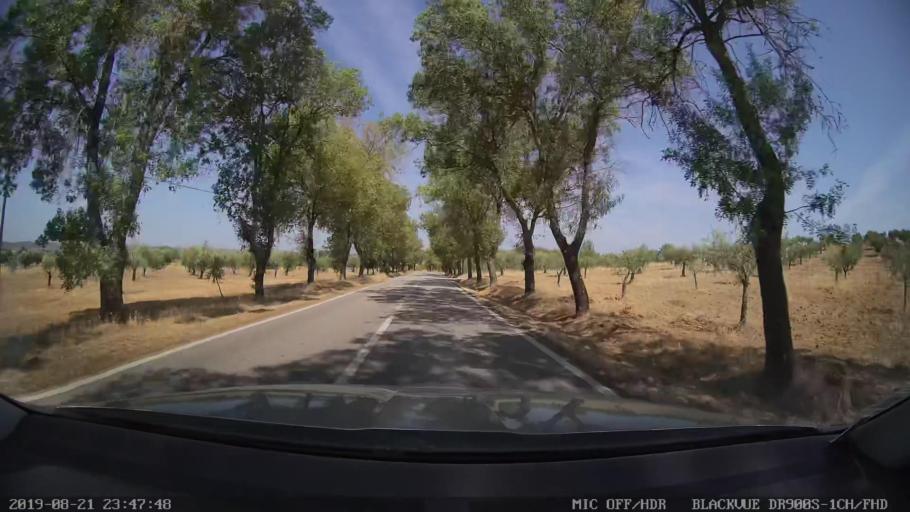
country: PT
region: Castelo Branco
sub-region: Idanha-A-Nova
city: Idanha-a-Nova
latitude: 39.8563
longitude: -7.2587
